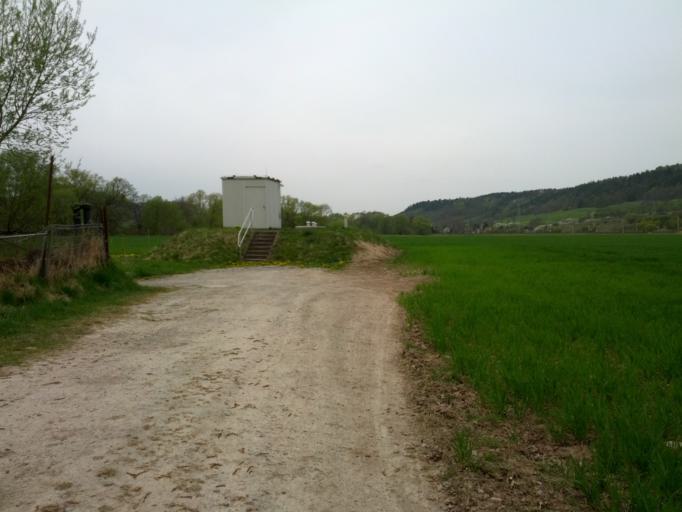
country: DE
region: Thuringia
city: Thal
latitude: 50.9599
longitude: 10.3810
